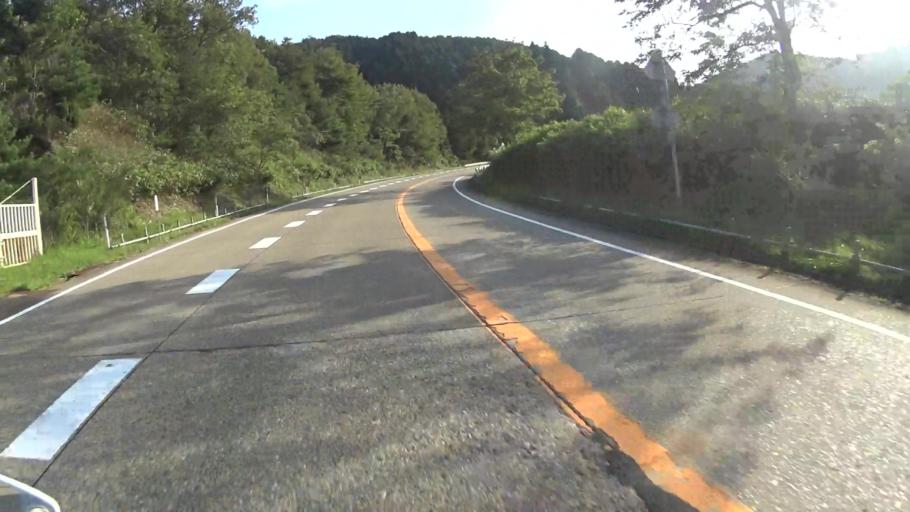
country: JP
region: Kyoto
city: Miyazu
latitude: 35.4536
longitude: 135.0790
